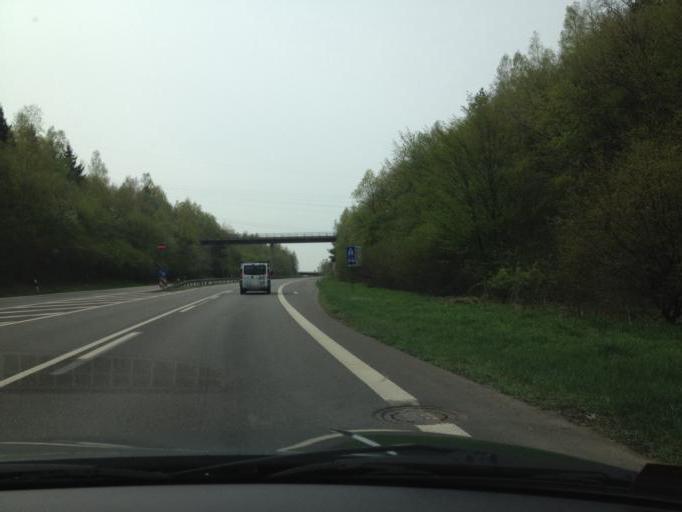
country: DE
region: Saarland
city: Neunkirchen
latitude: 49.3306
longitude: 7.1605
